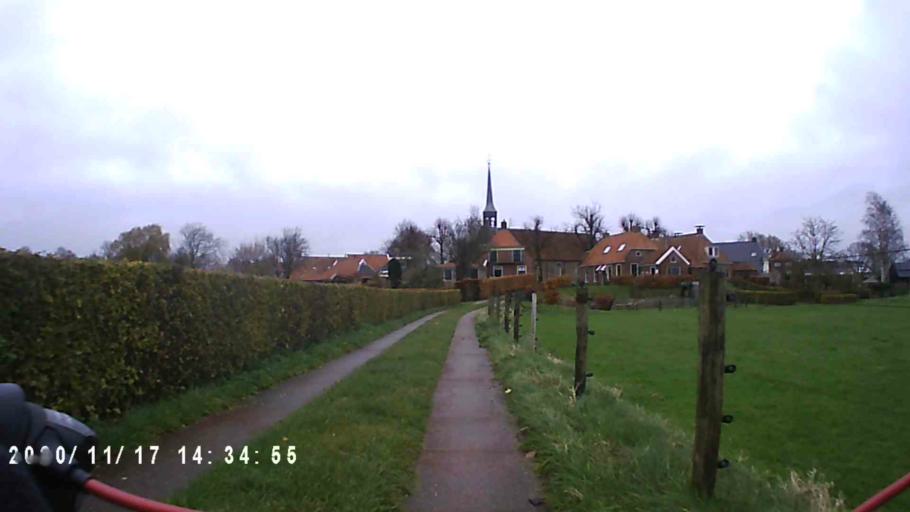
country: NL
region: Groningen
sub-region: Gemeente Zuidhorn
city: Oldehove
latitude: 53.2894
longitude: 6.3659
